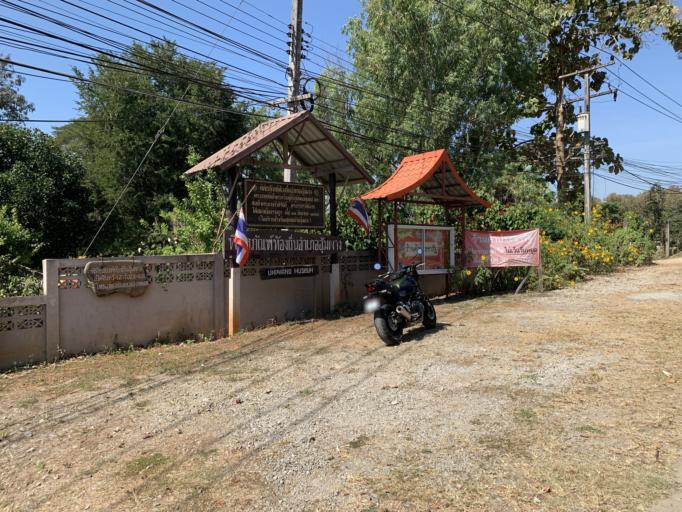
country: TH
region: Tak
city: Umphang
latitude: 16.0229
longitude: 98.8599
